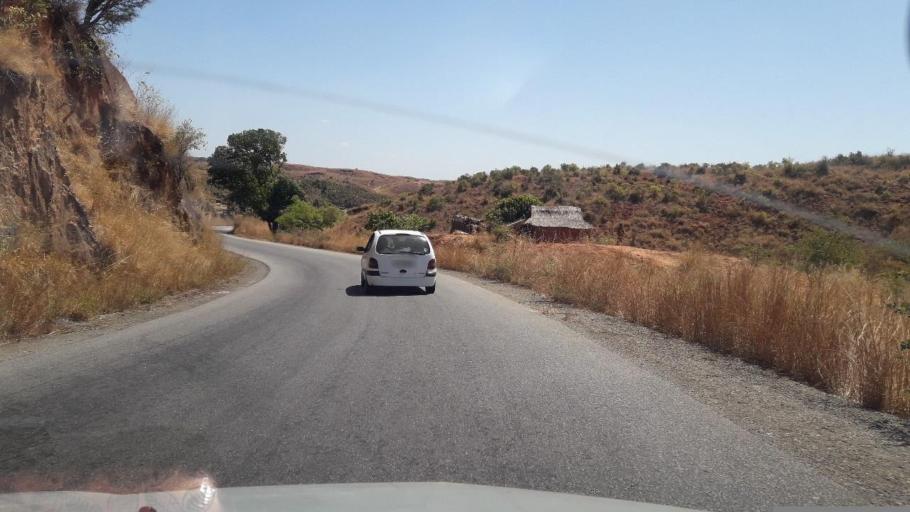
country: MG
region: Betsiboka
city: Maevatanana
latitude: -16.9406
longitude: 46.9565
